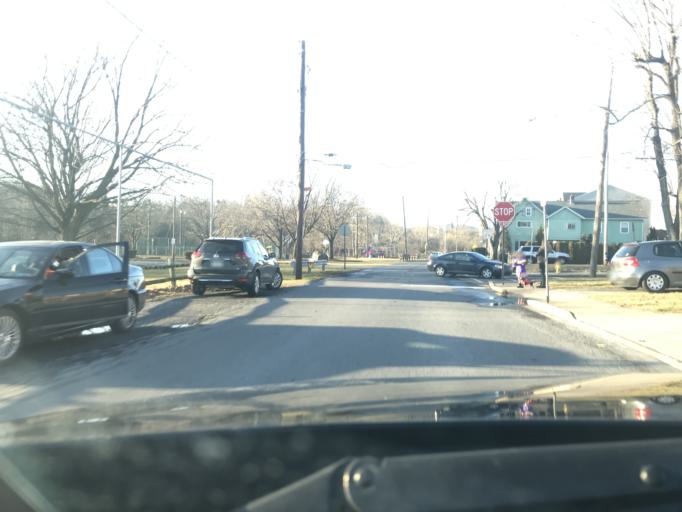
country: US
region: Pennsylvania
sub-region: Northampton County
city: Northampton
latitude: 40.6801
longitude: -75.4965
